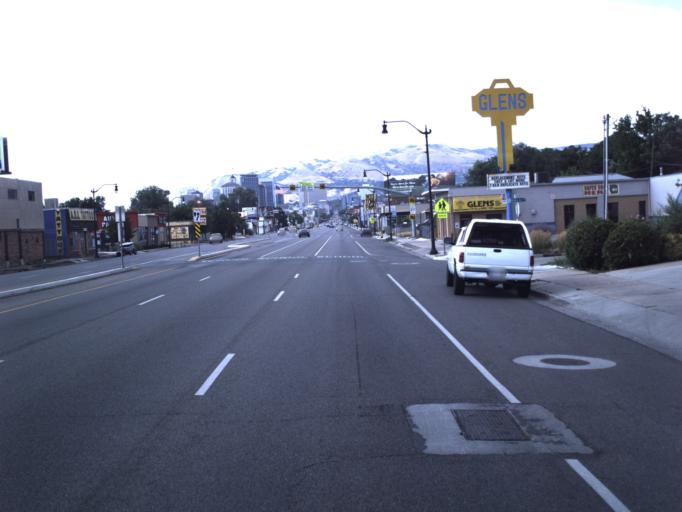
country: US
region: Utah
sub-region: Salt Lake County
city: Salt Lake City
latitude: 40.7433
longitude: -111.8881
